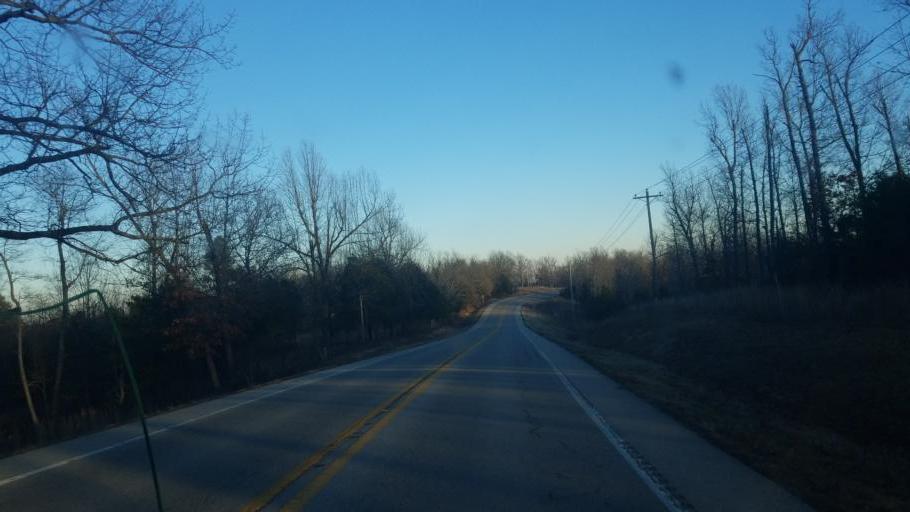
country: US
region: Arkansas
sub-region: Baxter County
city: Mountain Home
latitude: 36.3847
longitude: -92.1566
